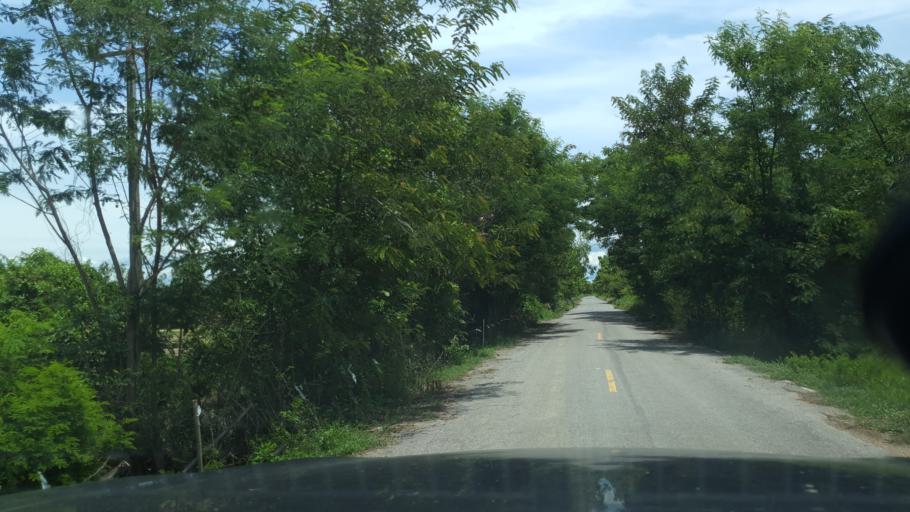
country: TH
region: Sukhothai
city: Ban Na
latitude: 17.1114
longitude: 99.6778
